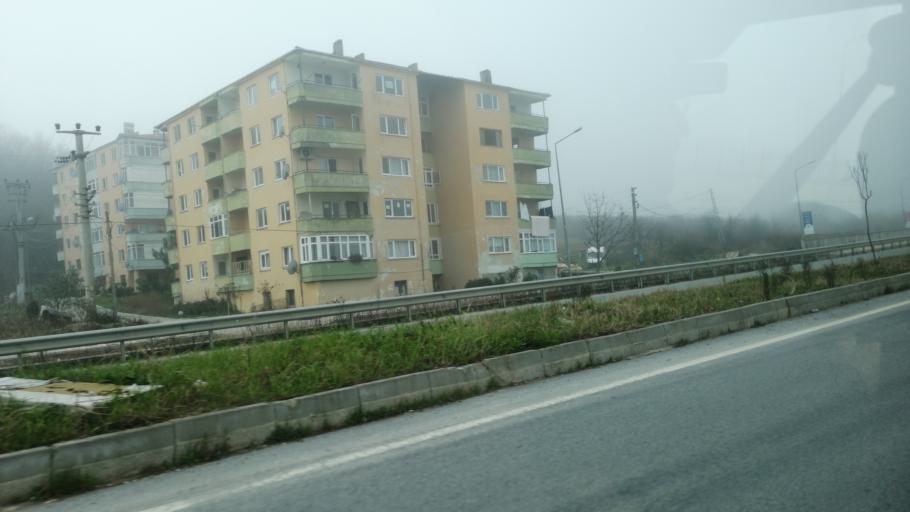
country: TR
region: Yalova
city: Kadikoy
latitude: 40.6507
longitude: 29.2241
